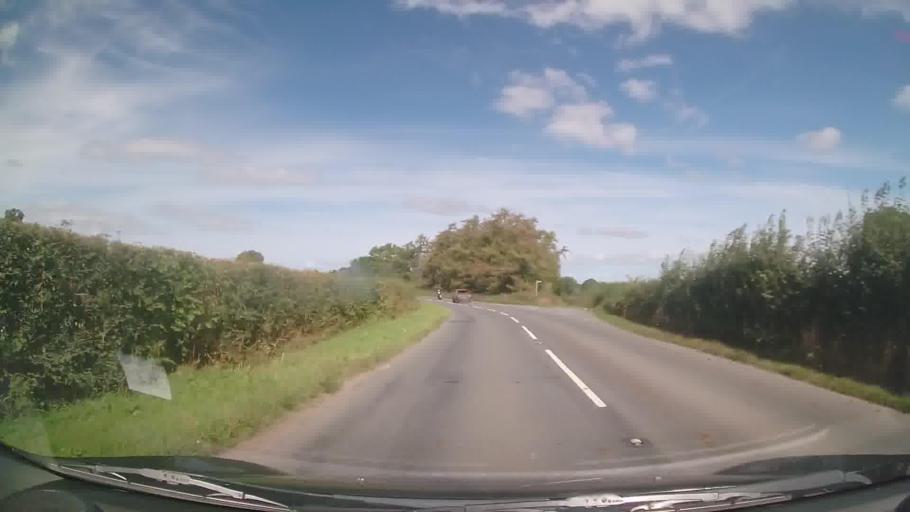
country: GB
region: England
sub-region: Herefordshire
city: Kington
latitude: 52.1521
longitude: -3.0124
